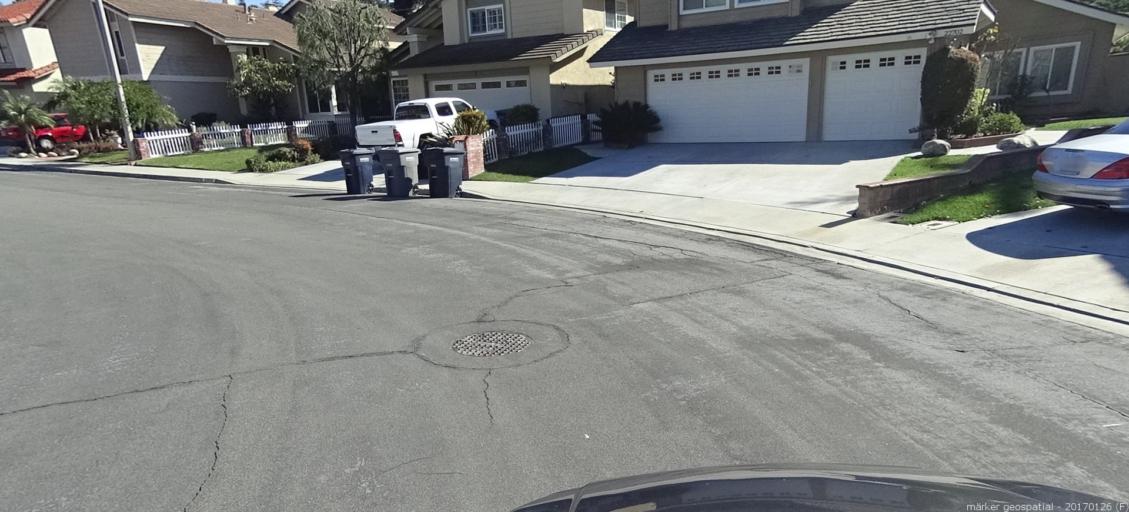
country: US
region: California
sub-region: Orange County
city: Lake Forest
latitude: 33.6329
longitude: -117.6747
